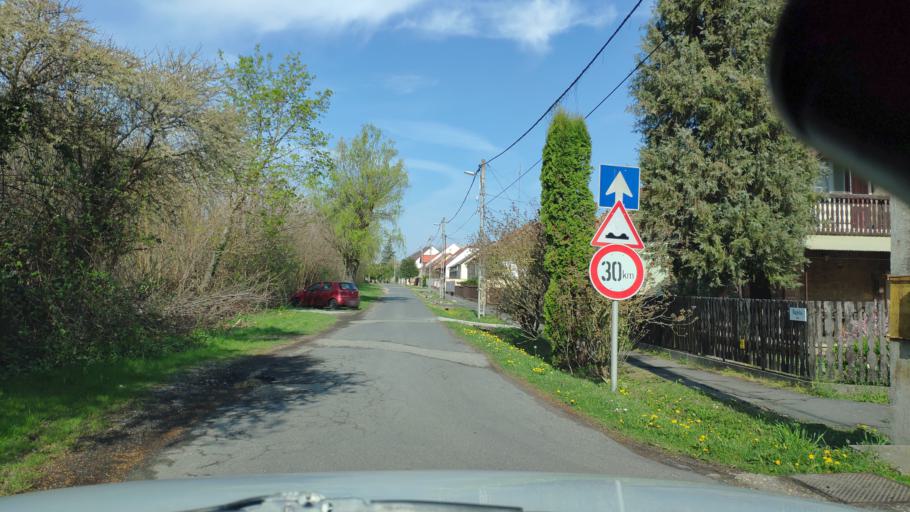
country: HU
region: Zala
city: Nagykanizsa
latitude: 46.4494
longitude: 17.0037
